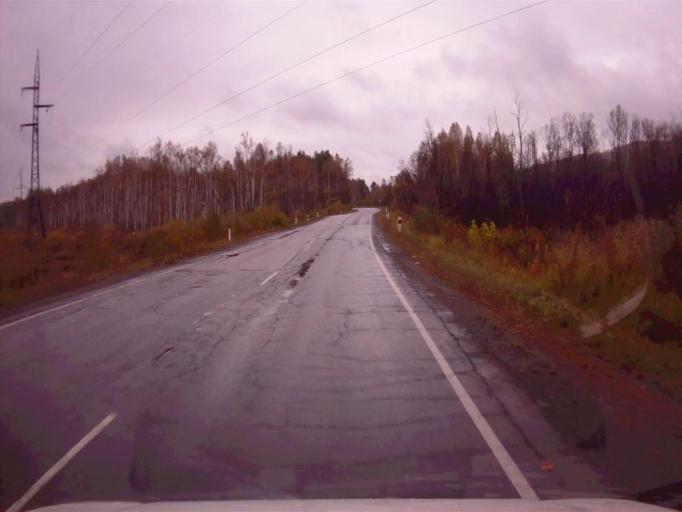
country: RU
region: Chelyabinsk
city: Verkhniy Ufaley
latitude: 55.9931
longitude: 60.3328
